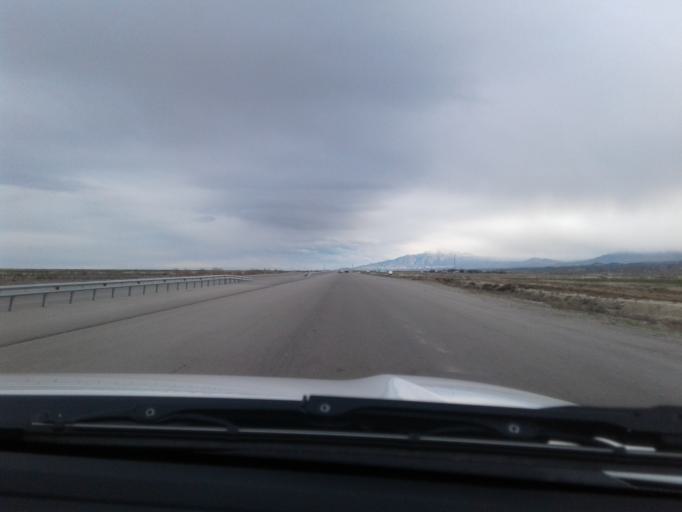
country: TM
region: Balkan
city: Serdar
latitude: 38.7944
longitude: 56.6939
